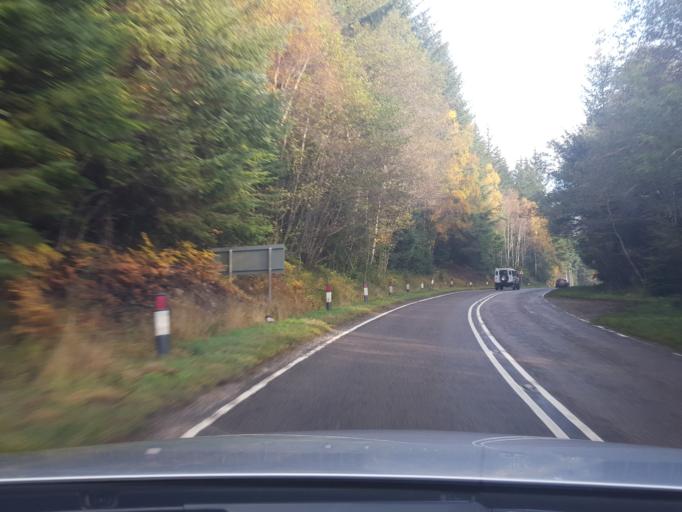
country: GB
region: Scotland
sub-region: Highland
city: Beauly
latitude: 57.2084
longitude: -4.6971
